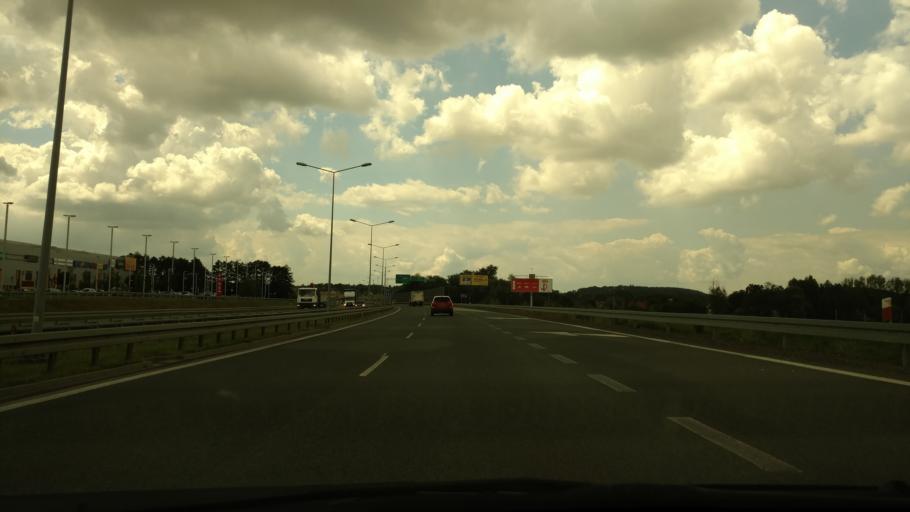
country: PL
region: Lesser Poland Voivodeship
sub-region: Powiat krakowski
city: Modlniczka
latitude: 50.1120
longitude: 19.8454
